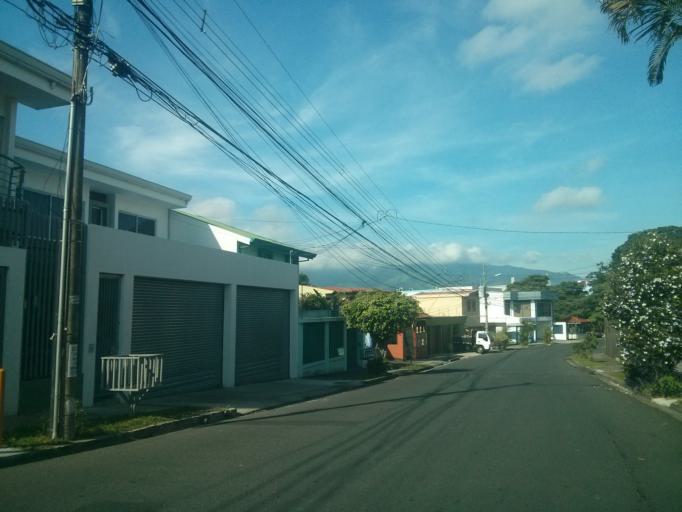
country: CR
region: San Jose
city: San Pedro
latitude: 9.9269
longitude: -84.0532
